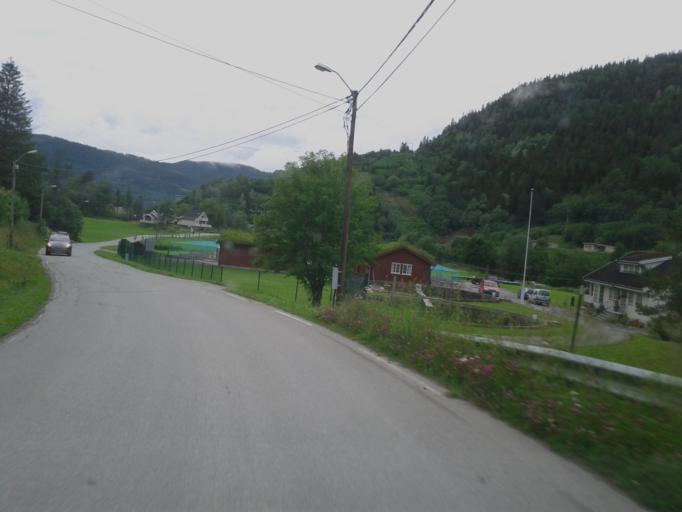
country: NO
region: Sor-Trondelag
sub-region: Melhus
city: Lundamo
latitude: 63.1453
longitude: 10.3213
